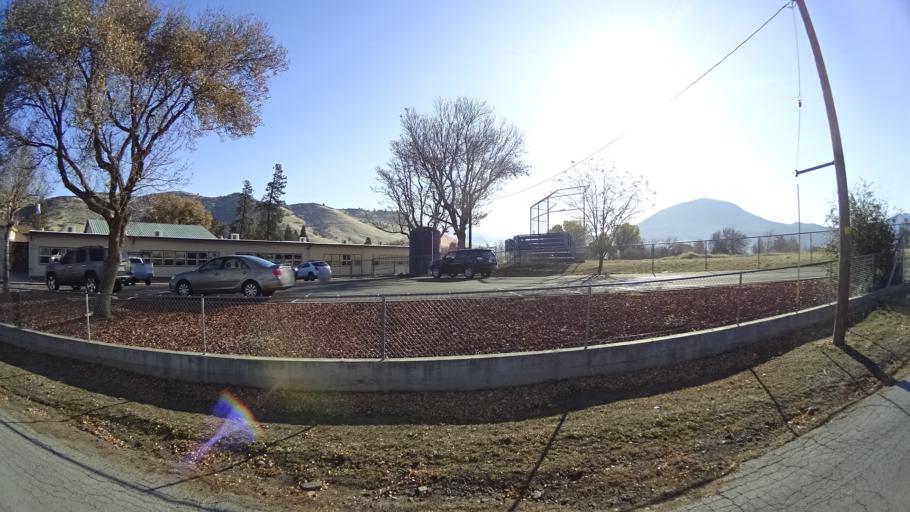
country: US
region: California
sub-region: Siskiyou County
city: Montague
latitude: 41.9109
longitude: -122.5620
